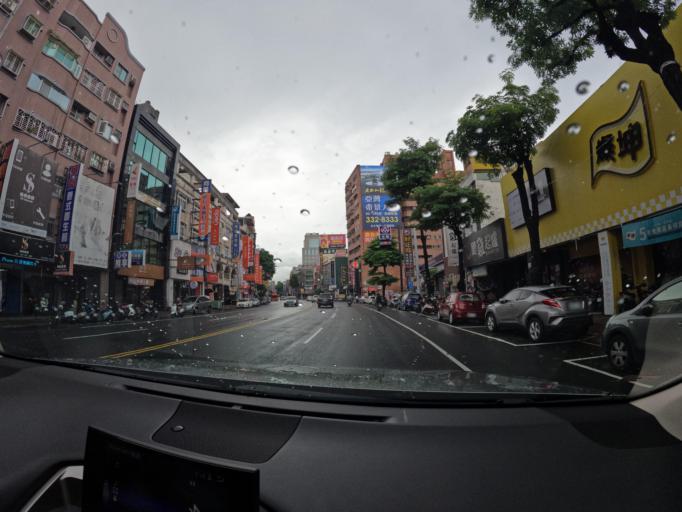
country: TW
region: Kaohsiung
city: Kaohsiung
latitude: 22.6644
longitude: 120.3082
